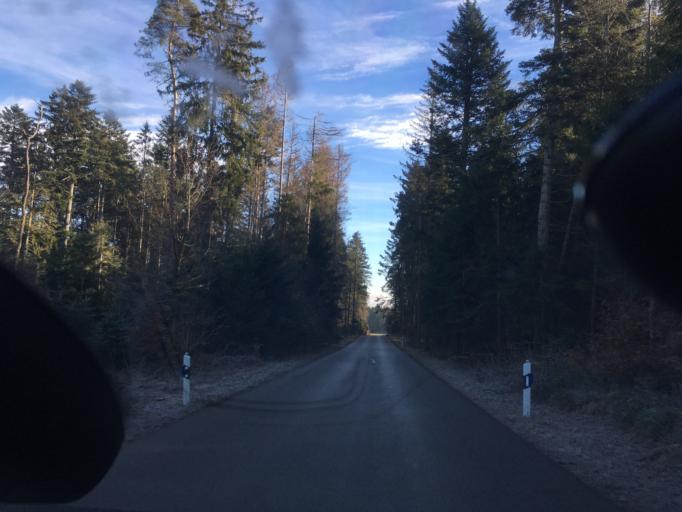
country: DE
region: Baden-Wuerttemberg
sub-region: Freiburg Region
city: Herrischried
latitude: 47.6548
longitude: 8.0363
